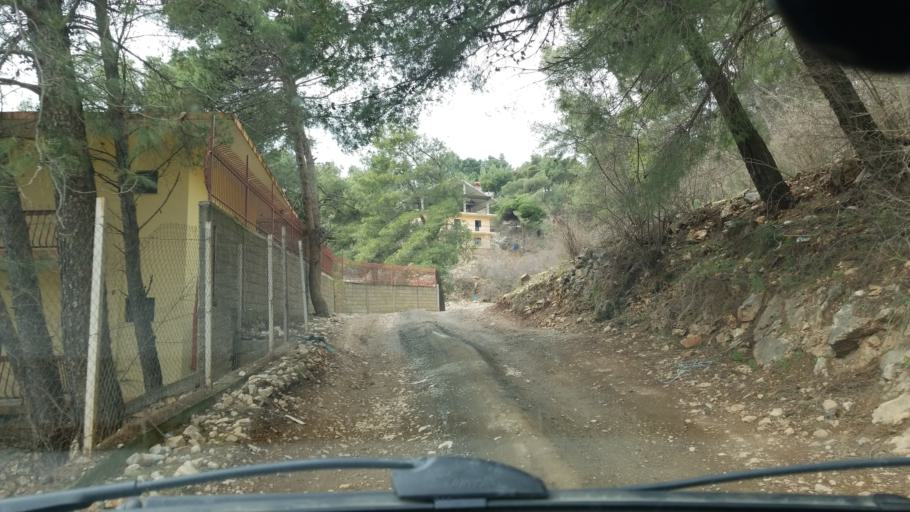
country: AL
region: Lezhe
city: Shengjin
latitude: 41.8166
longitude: 19.5846
